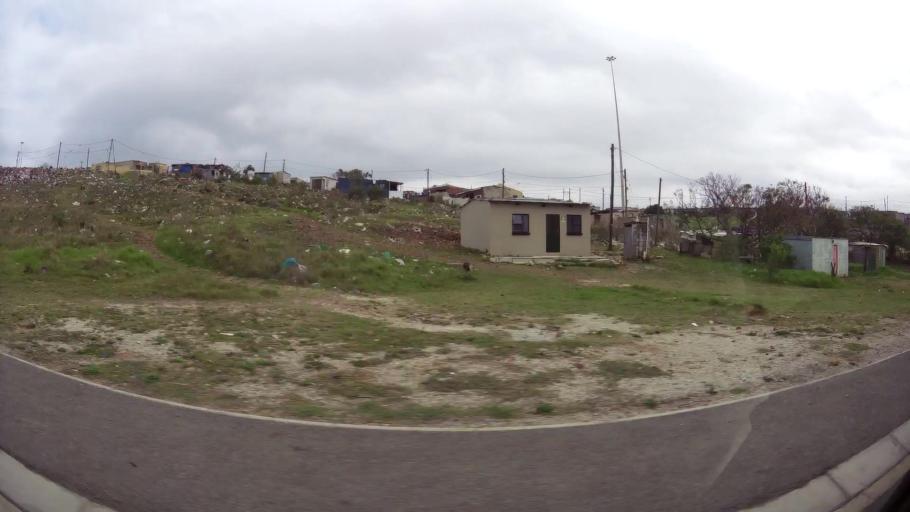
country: ZA
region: Eastern Cape
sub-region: Nelson Mandela Bay Metropolitan Municipality
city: Port Elizabeth
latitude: -33.9120
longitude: 25.5389
